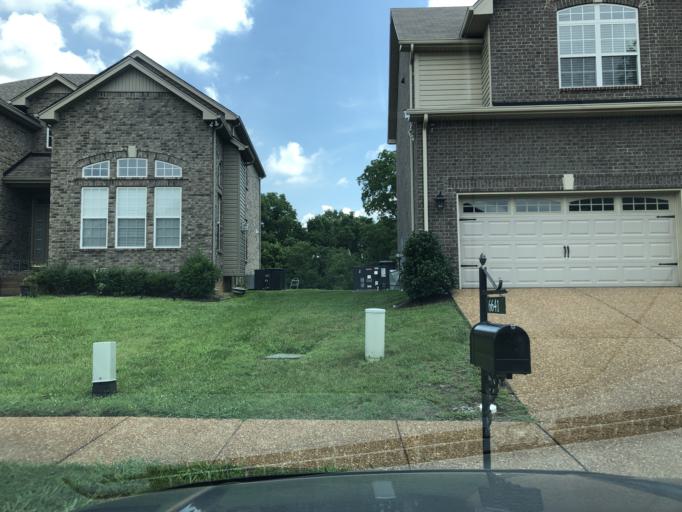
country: US
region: Tennessee
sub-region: Williamson County
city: Nolensville
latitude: 36.0162
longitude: -86.6909
